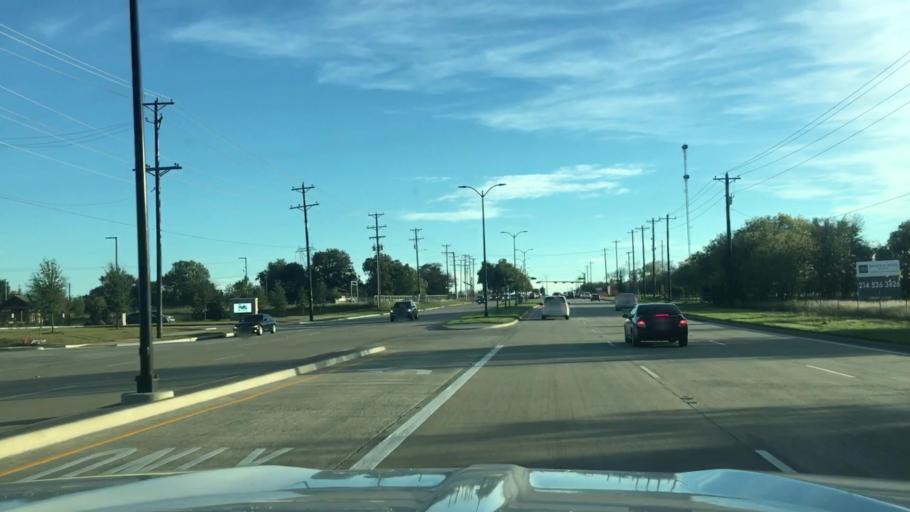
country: US
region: Texas
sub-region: Collin County
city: Prosper
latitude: 33.2071
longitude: -96.8028
